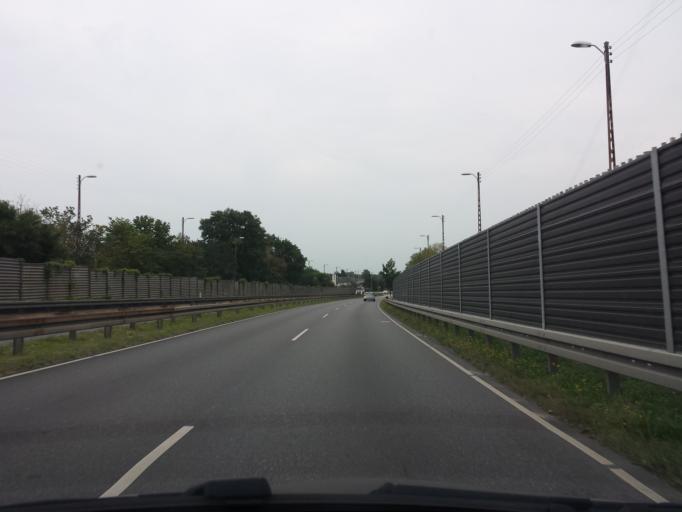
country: DK
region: Capital Region
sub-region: Herlev Kommune
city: Herlev
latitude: 55.7190
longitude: 12.4399
